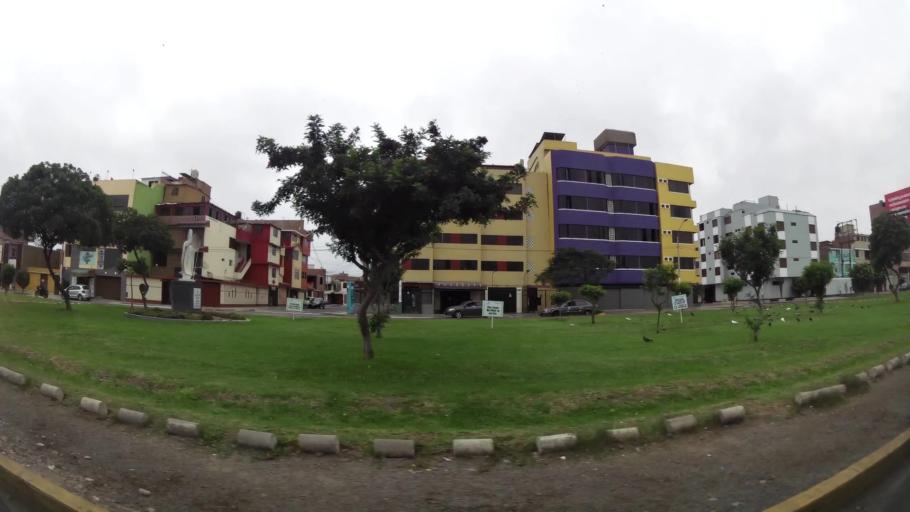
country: PE
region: Callao
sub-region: Callao
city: Callao
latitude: -12.0695
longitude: -77.1110
